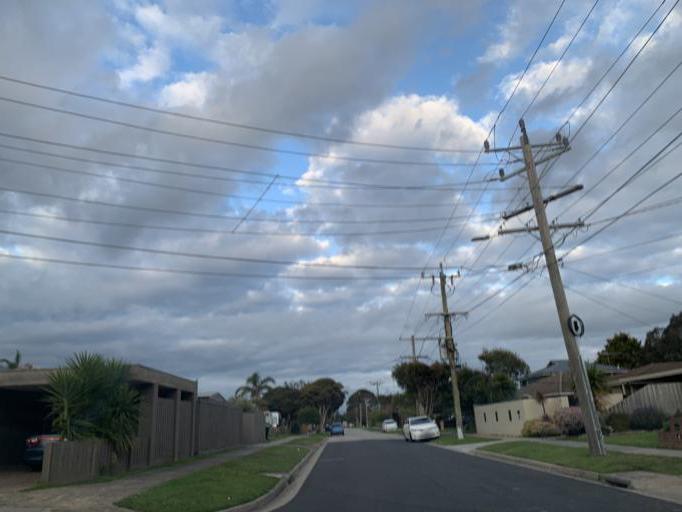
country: AU
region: Victoria
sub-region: Kingston
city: Aspendale
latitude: -38.0220
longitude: 145.1056
